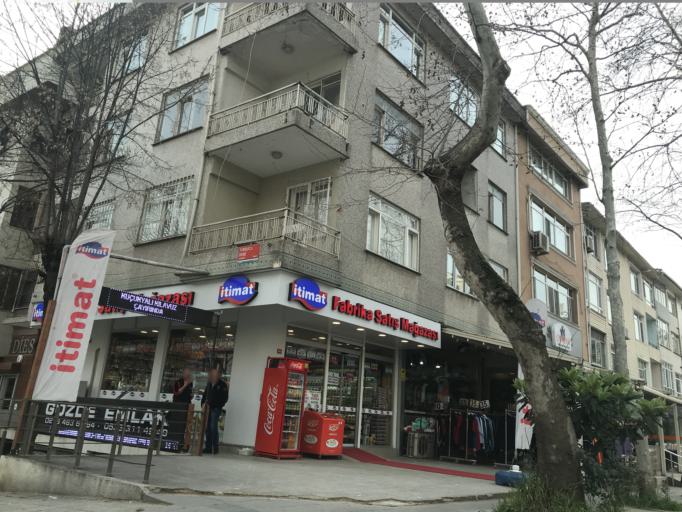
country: TR
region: Istanbul
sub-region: Atasehir
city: Atasehir
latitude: 40.9616
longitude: 29.0926
